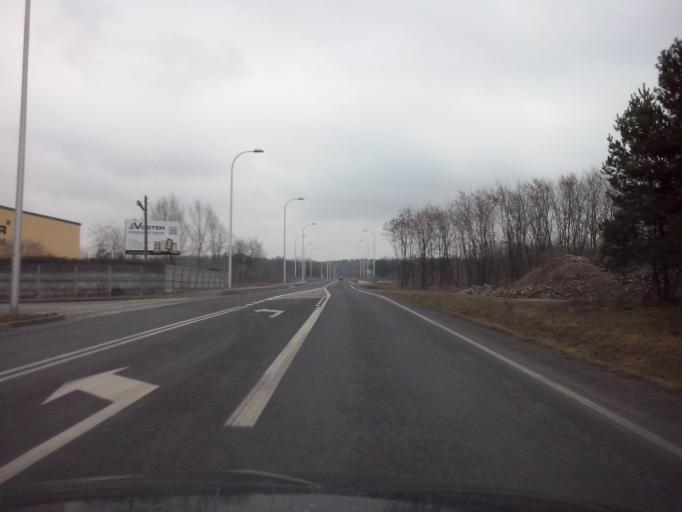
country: PL
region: Subcarpathian Voivodeship
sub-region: Powiat nizanski
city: Przedzel
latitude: 50.5176
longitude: 22.2255
